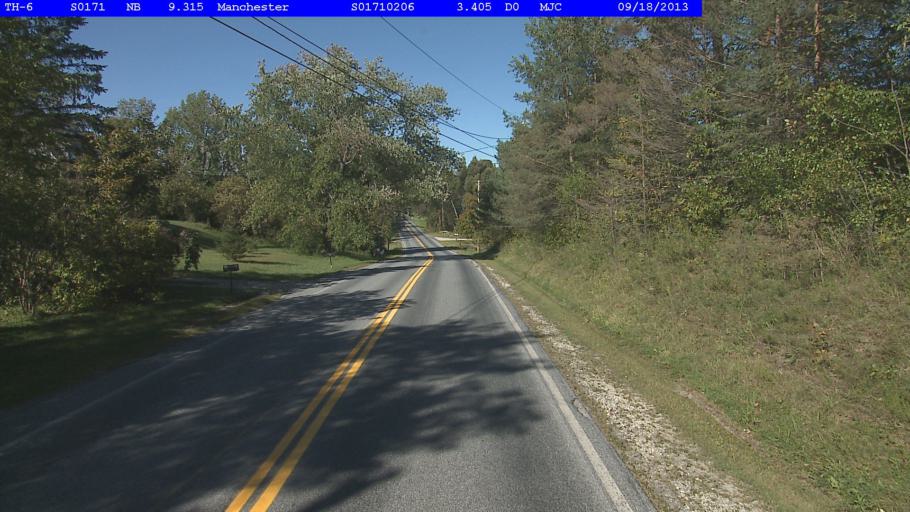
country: US
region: Vermont
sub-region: Bennington County
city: Manchester Center
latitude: 43.1536
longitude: -73.0518
